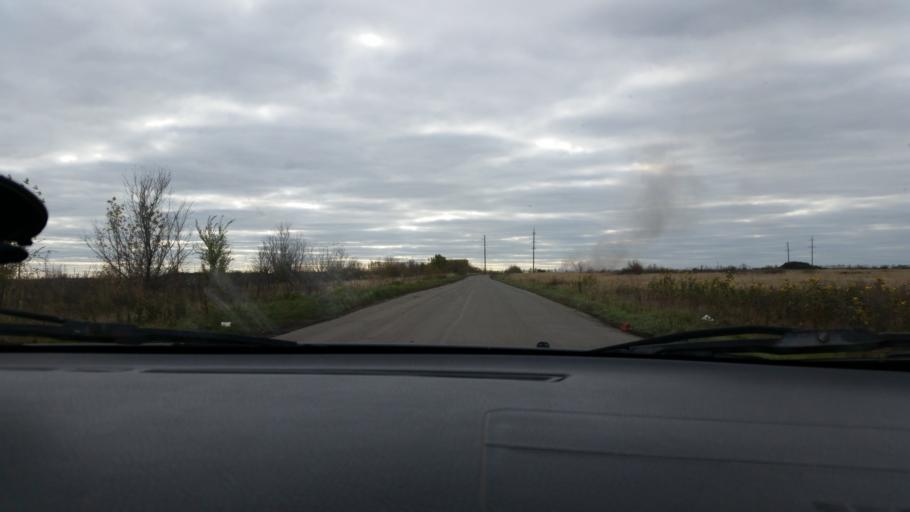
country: RU
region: Lipetsk
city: Gryazi
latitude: 52.4657
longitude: 39.9341
